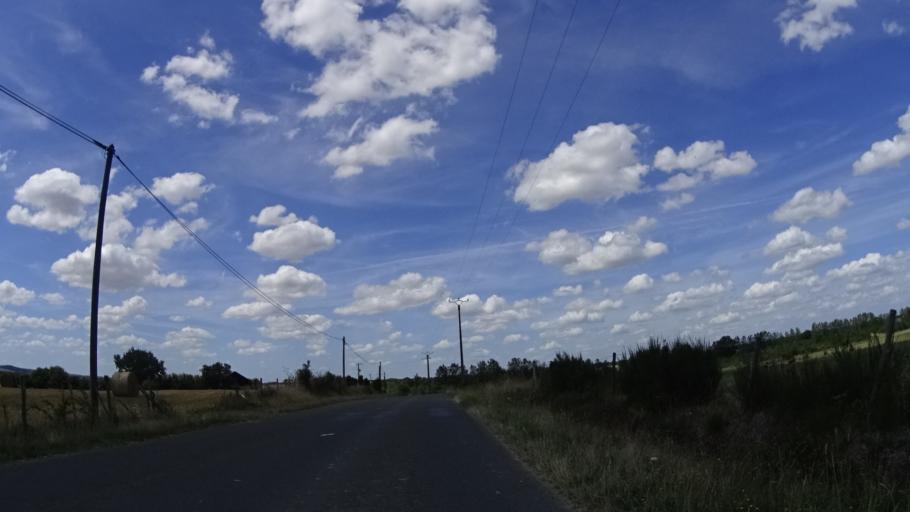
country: FR
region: Pays de la Loire
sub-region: Departement de Maine-et-Loire
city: Segre
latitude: 47.6100
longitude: -0.9104
